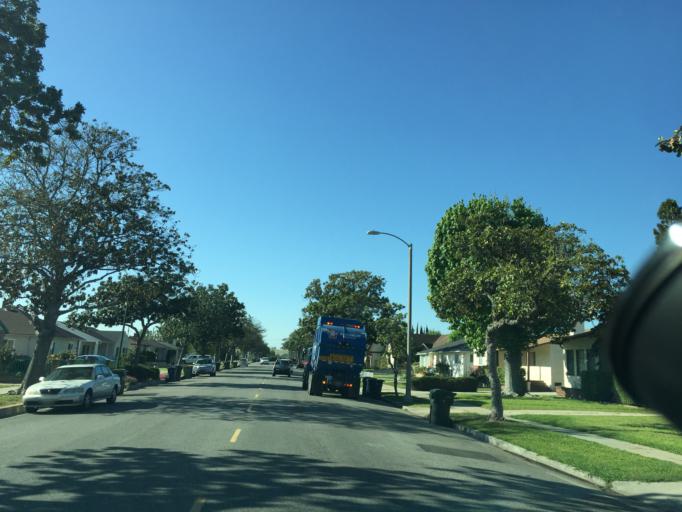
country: US
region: California
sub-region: Los Angeles County
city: Monterey Park
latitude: 34.0755
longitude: -118.1169
